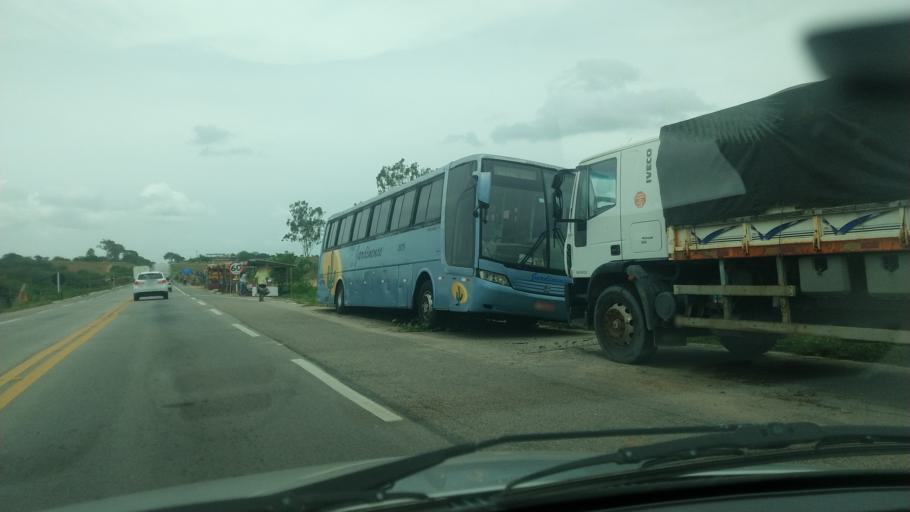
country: BR
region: Rio Grande do Norte
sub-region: Santa Cruz
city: Santa Cruz
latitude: -6.2116
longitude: -36.1810
